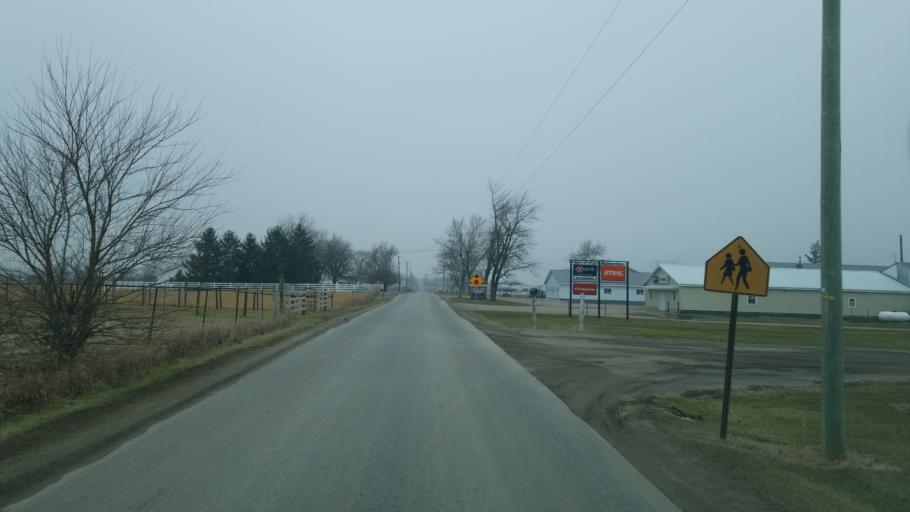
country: US
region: Indiana
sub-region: Adams County
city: Berne
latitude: 40.7016
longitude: -84.9504
